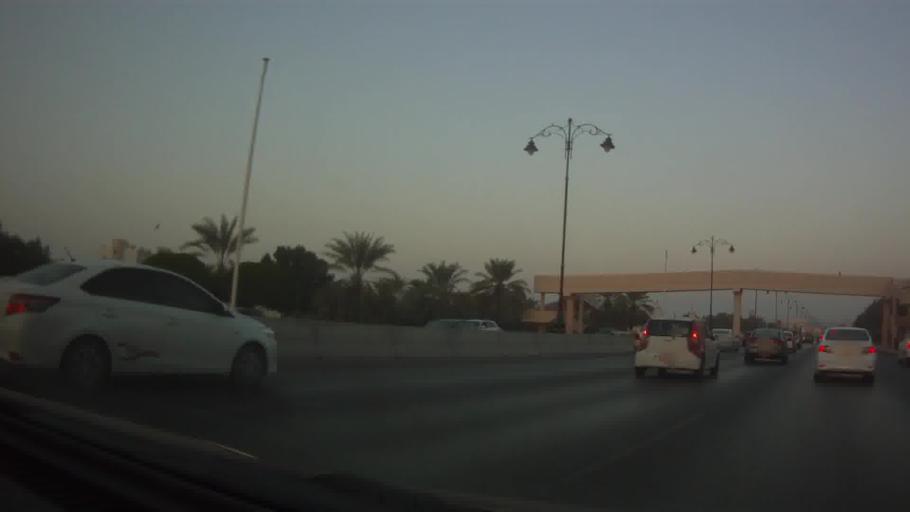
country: OM
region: Muhafazat Masqat
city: Bawshar
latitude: 23.5971
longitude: 58.4220
